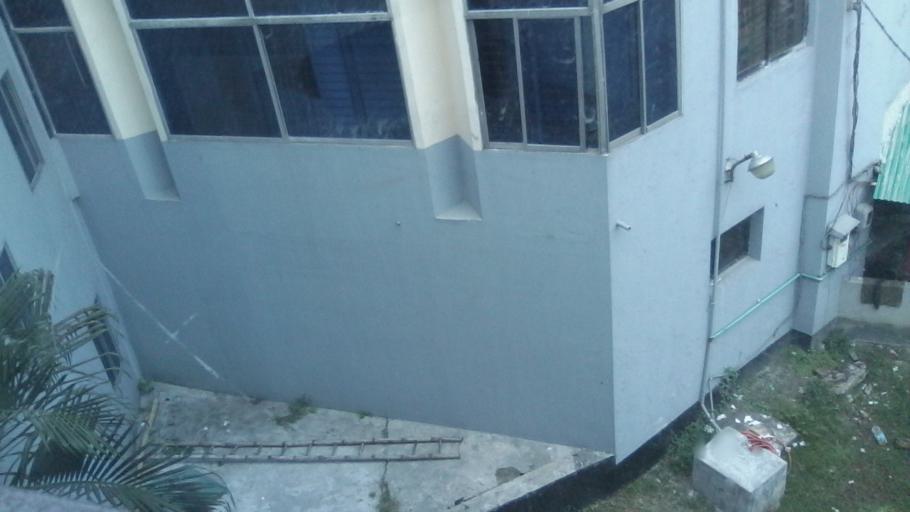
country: BD
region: Rajshahi
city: Bogra
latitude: 24.8095
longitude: 89.3825
